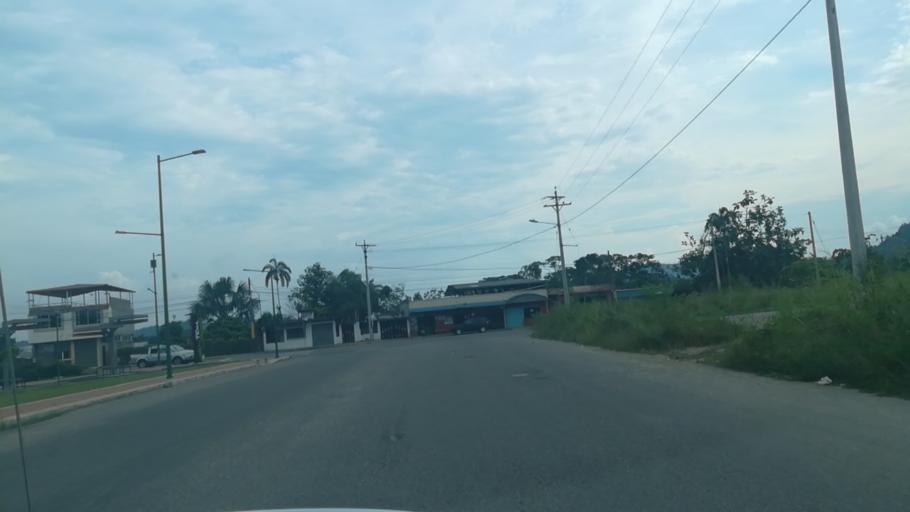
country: EC
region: Napo
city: Tena
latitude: -0.9855
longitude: -77.8244
